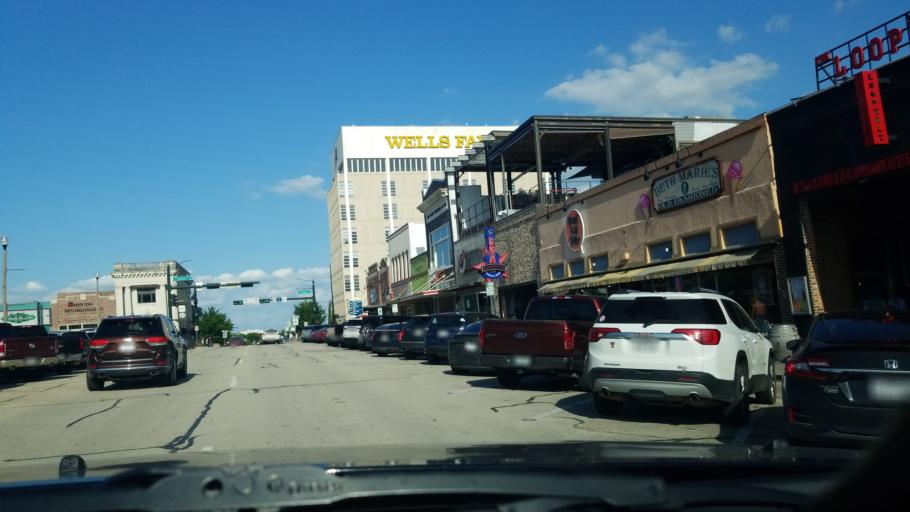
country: US
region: Texas
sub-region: Denton County
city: Denton
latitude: 33.2145
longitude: -97.1335
